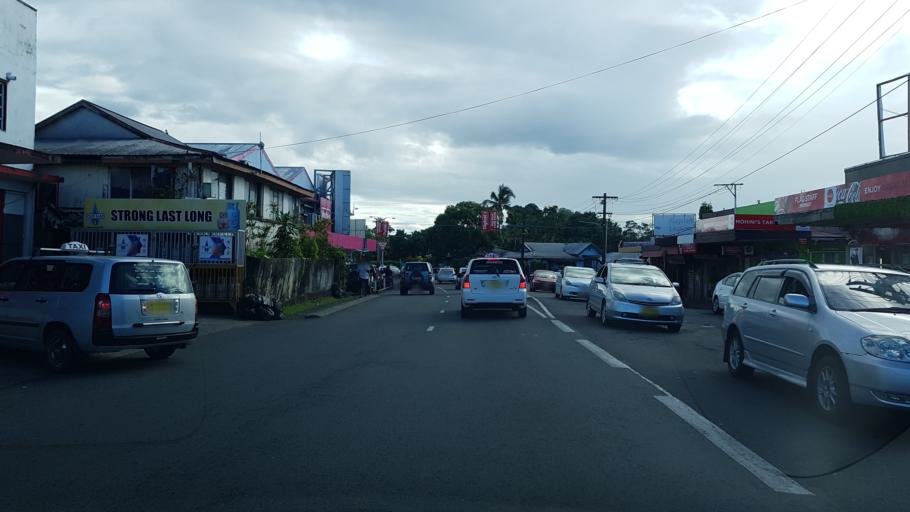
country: FJ
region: Central
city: Suva
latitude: -18.1446
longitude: 178.4355
